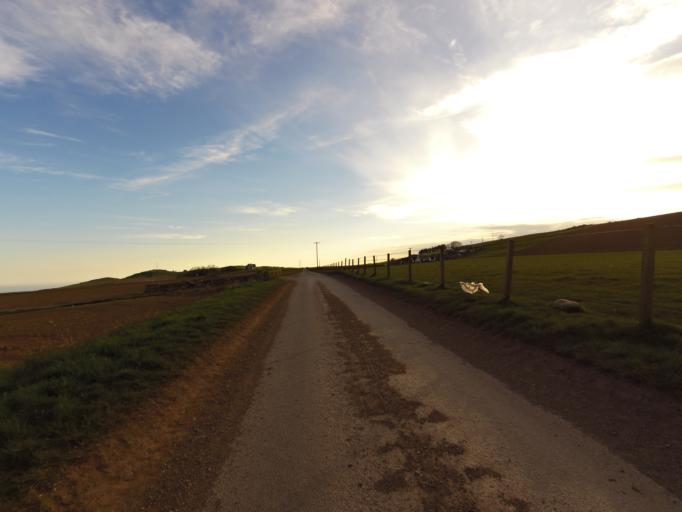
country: GB
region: Scotland
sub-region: Aberdeenshire
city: Inverbervie
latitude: 56.8648
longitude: -2.2496
